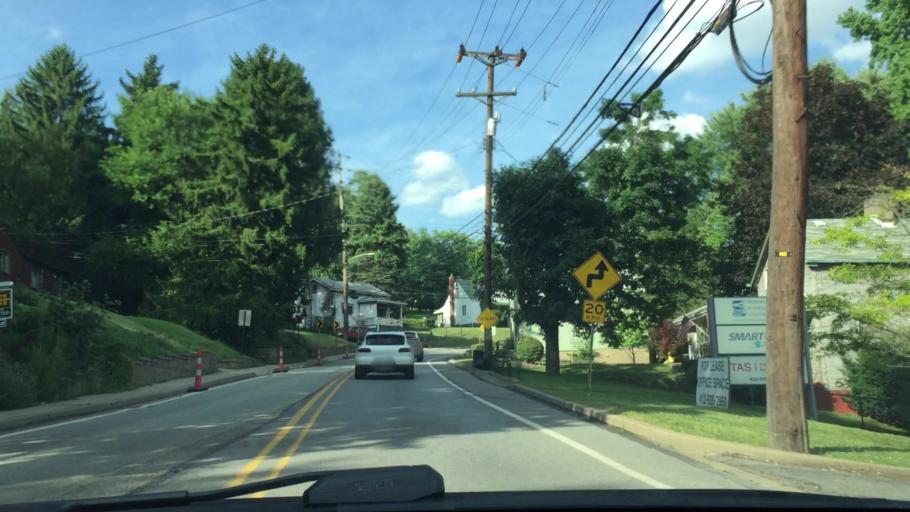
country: US
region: Pennsylvania
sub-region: Allegheny County
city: Green Tree
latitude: 40.4212
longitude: -80.0529
